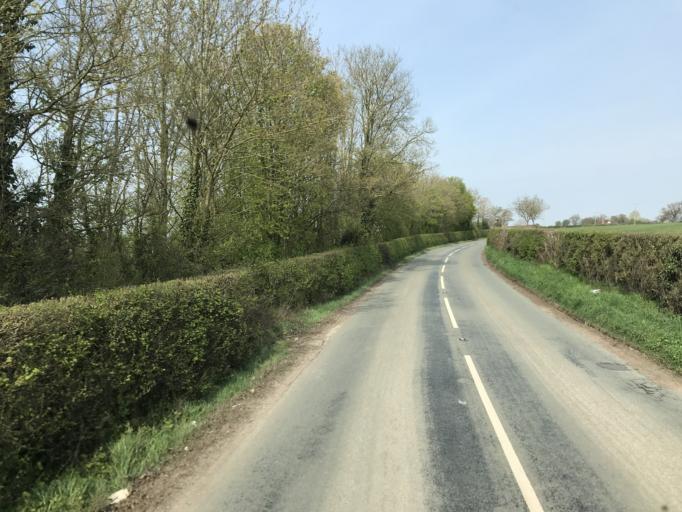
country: GB
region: England
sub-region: Cheshire West and Chester
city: Eccleston
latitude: 53.1533
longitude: -2.8623
